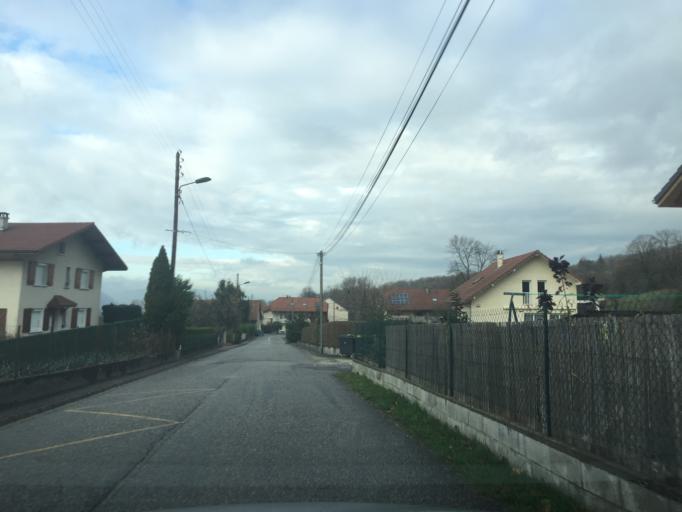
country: FR
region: Rhone-Alpes
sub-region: Departement de la Savoie
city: Mouxy
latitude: 45.6973
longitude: 5.9333
